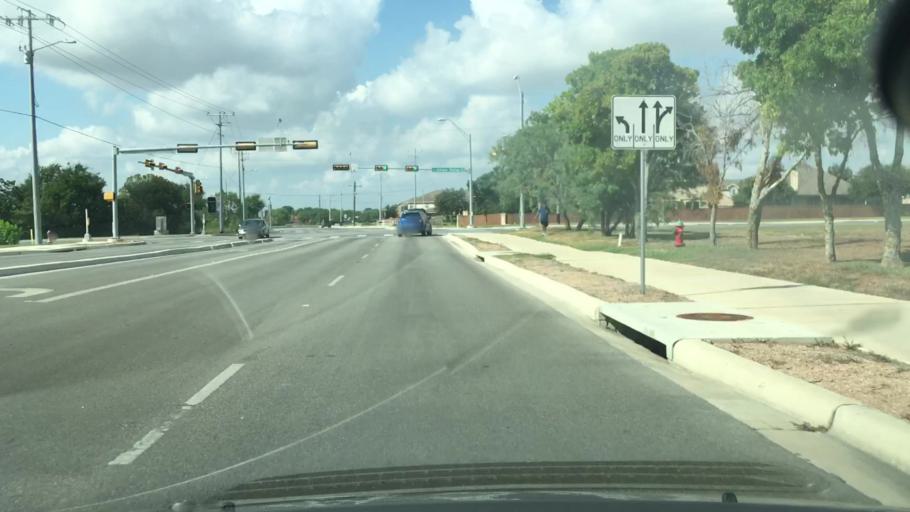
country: US
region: Texas
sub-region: Guadalupe County
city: Cibolo
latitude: 29.5726
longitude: -98.2397
